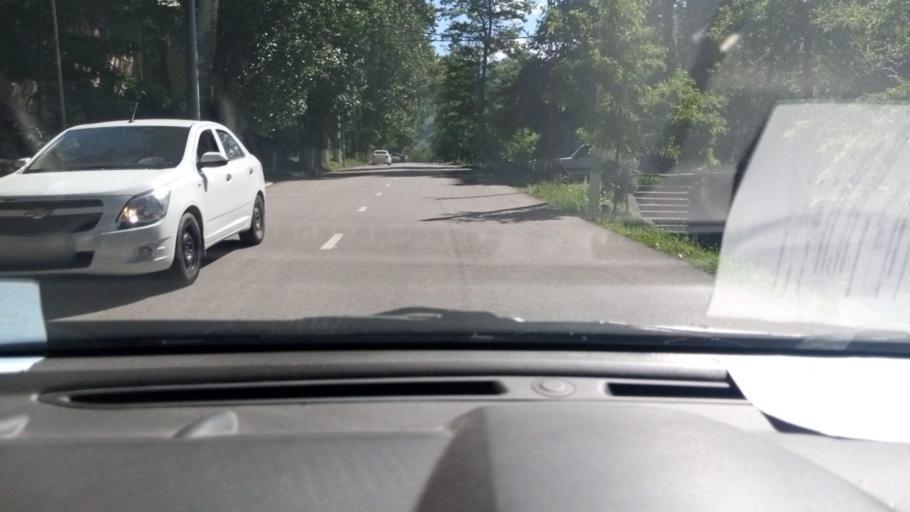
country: UZ
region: Toshkent
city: Yangiobod
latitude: 41.1204
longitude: 70.0968
